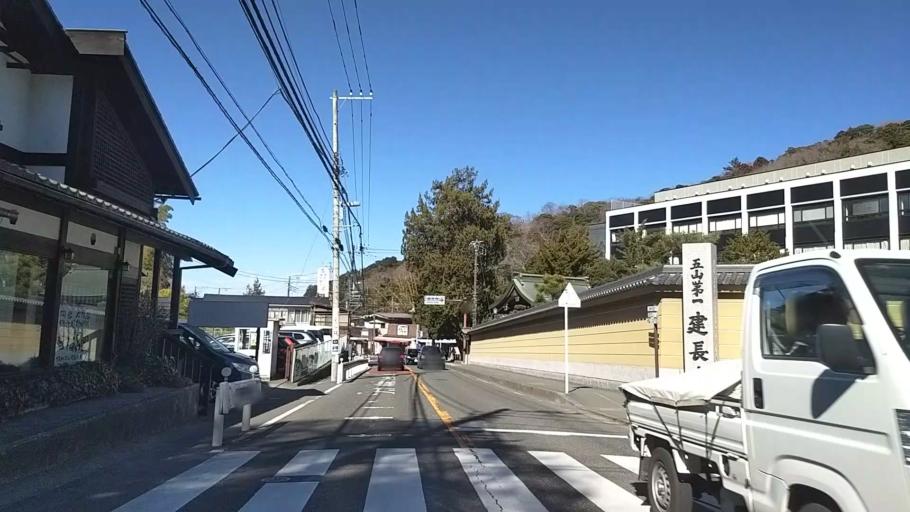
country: JP
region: Kanagawa
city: Kamakura
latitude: 35.3302
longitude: 139.5530
